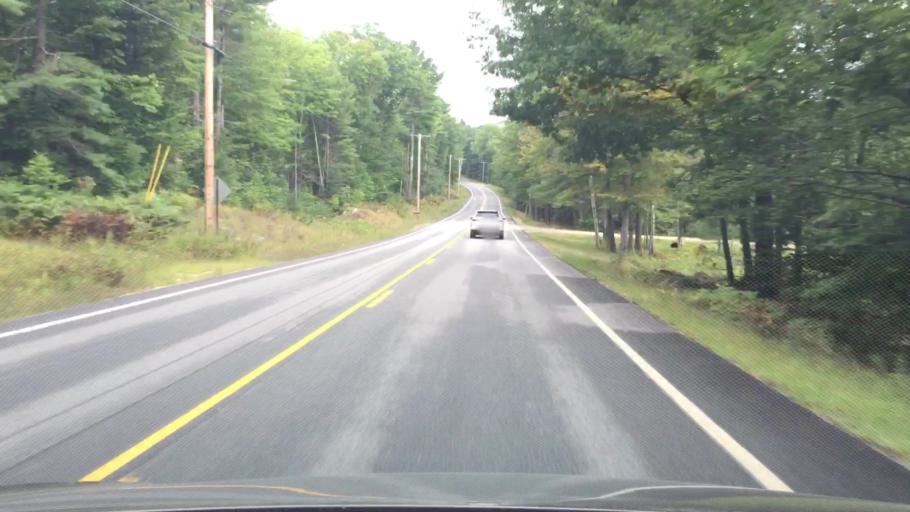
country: US
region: Maine
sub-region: Oxford County
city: Hartford
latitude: 44.3514
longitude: -70.3021
